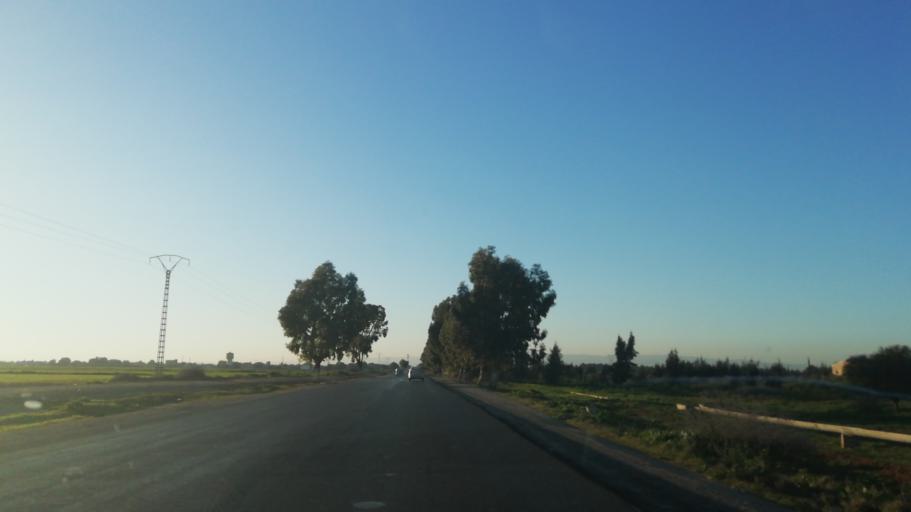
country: DZ
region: Relizane
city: Relizane
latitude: 35.7624
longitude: 0.6510
